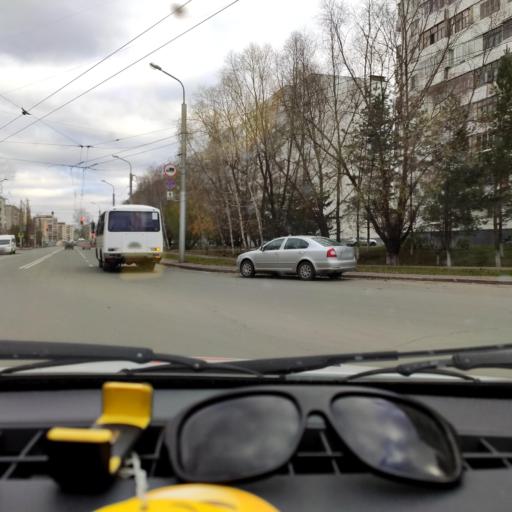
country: RU
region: Bashkortostan
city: Ufa
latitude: 54.7744
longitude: 56.1126
